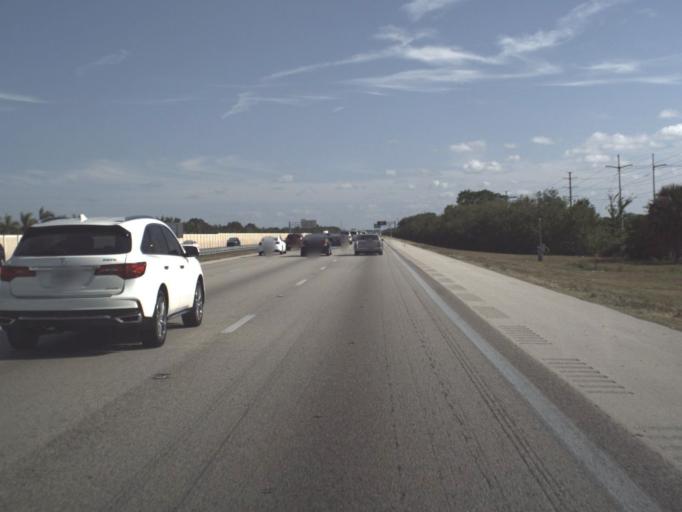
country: US
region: Florida
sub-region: Brevard County
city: June Park
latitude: 28.1071
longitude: -80.7061
